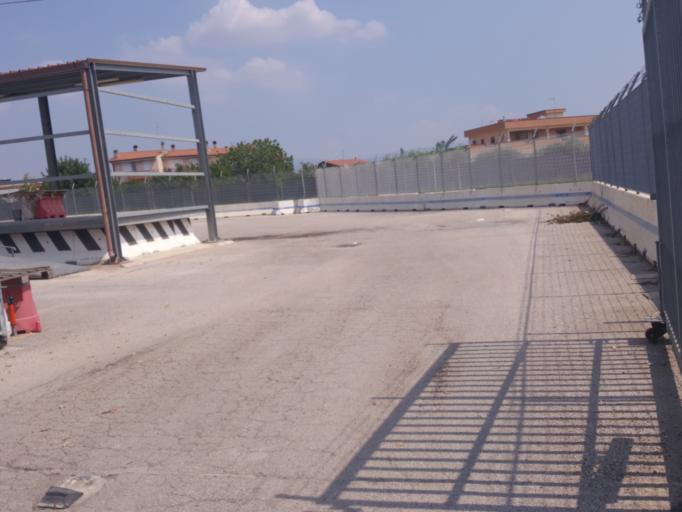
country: IT
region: Latium
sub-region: Provincia di Latina
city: Aprilia
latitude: 41.5787
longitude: 12.6559
